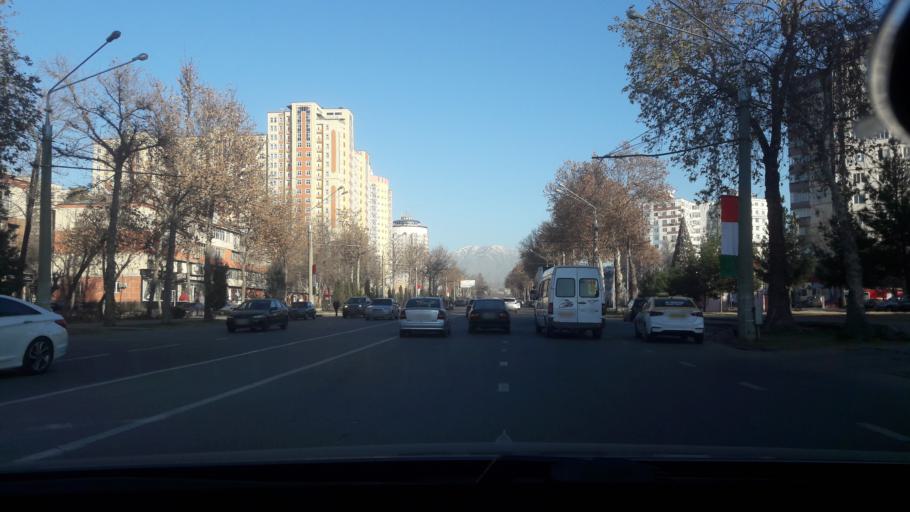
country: TJ
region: Dushanbe
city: Dushanbe
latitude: 38.5595
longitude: 68.7550
